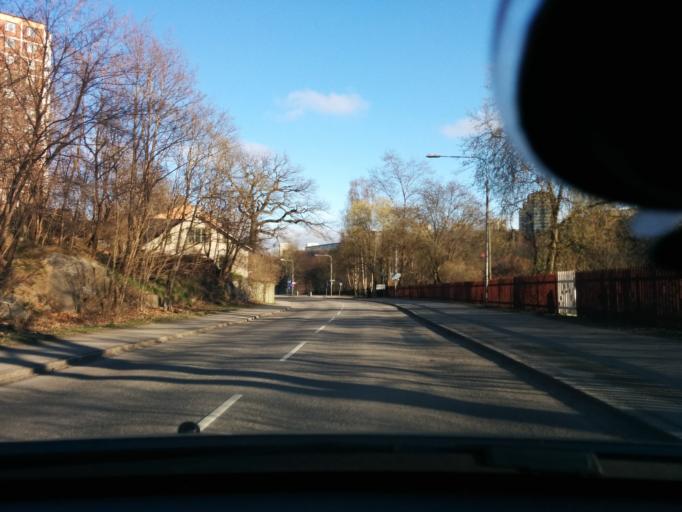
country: SE
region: Stockholm
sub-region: Stockholms Kommun
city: Arsta
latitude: 59.3139
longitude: 18.0086
